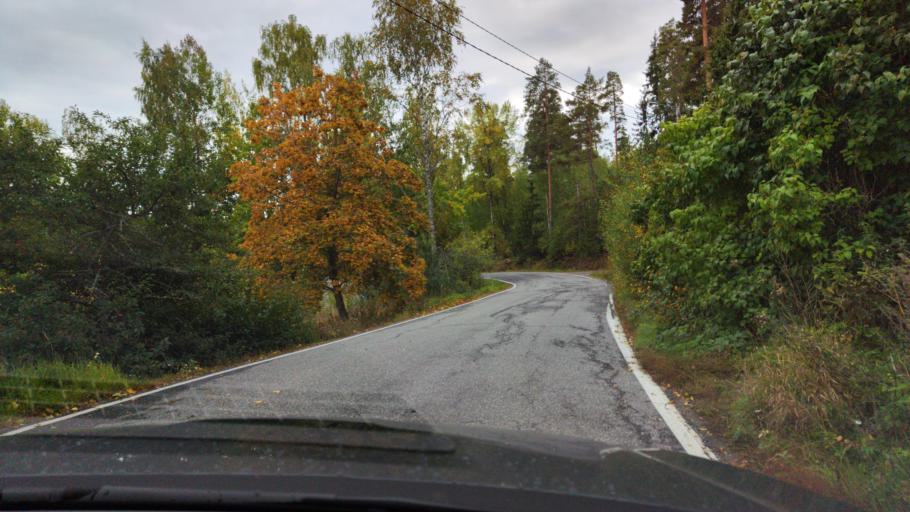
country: FI
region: Varsinais-Suomi
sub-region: Aboland-Turunmaa
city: Pargas
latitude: 60.3623
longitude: 22.2794
